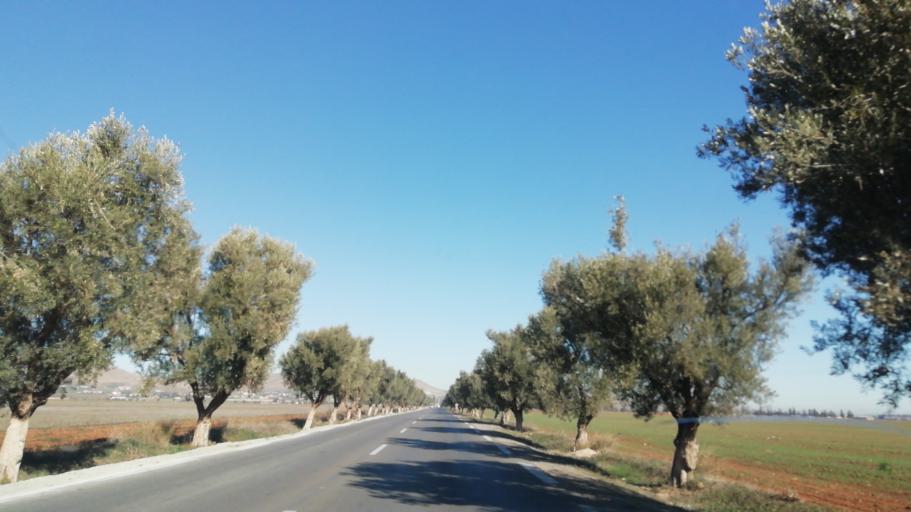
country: DZ
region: Mascara
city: Bou Hanifia el Hamamat
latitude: 35.2028
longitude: 0.1091
